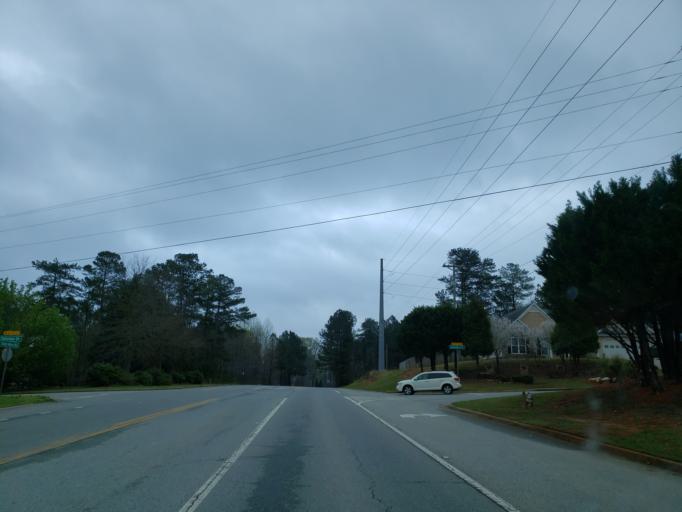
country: US
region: Georgia
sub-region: Polk County
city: Rockmart
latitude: 33.9241
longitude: -84.9863
